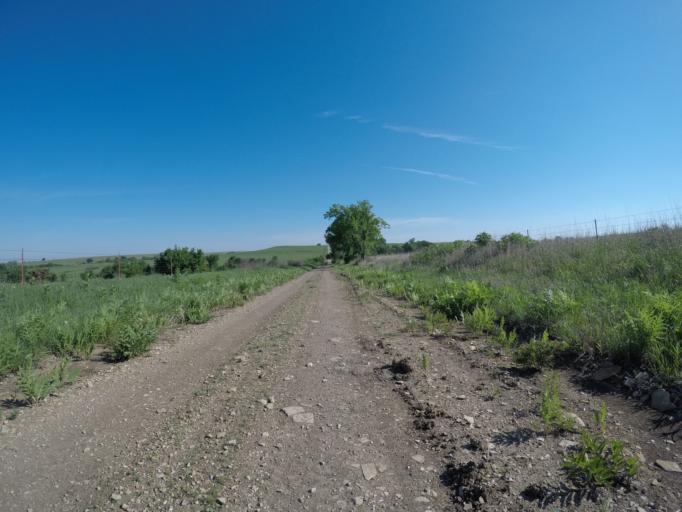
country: US
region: Kansas
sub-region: Wabaunsee County
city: Alma
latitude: 38.8792
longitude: -96.1136
